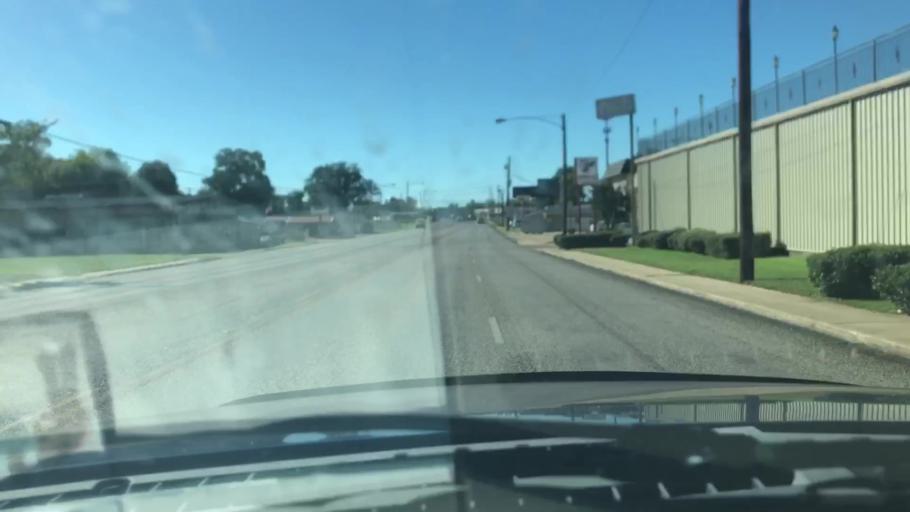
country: US
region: Texas
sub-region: Bowie County
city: Texarkana
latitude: 33.4378
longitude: -94.0533
